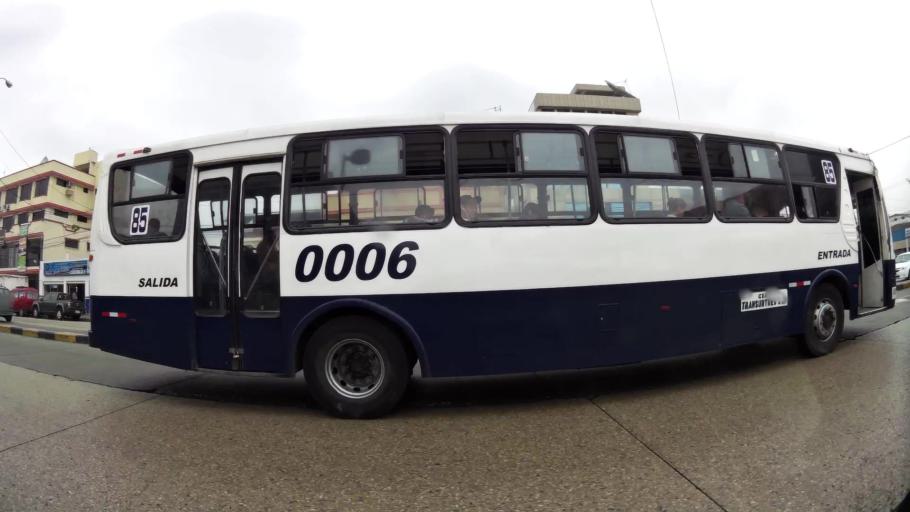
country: EC
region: Guayas
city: Eloy Alfaro
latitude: -2.1512
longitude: -79.8930
